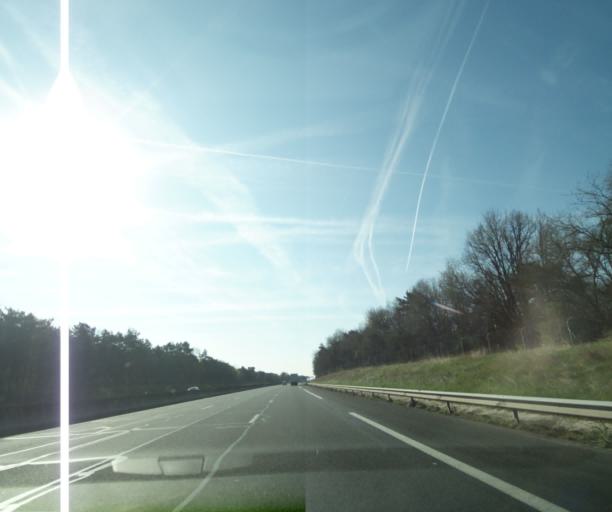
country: FR
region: Ile-de-France
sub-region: Departement de Seine-et-Marne
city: Bagneaux-sur-Loing
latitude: 48.2409
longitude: 2.7490
